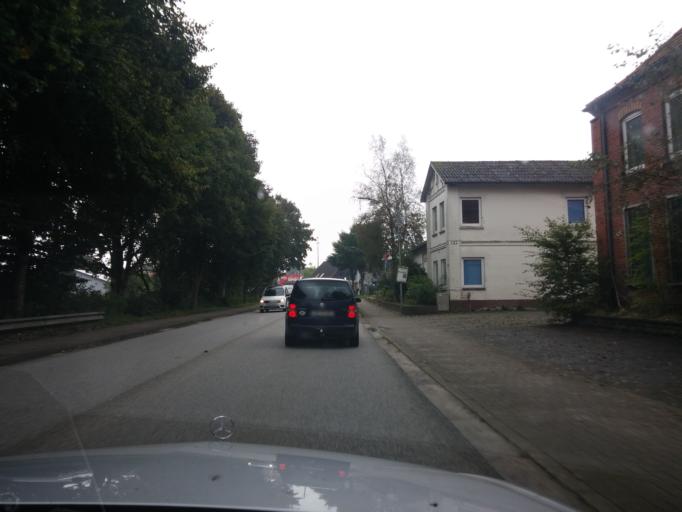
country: DE
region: Schleswig-Holstein
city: Treia
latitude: 54.5144
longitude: 9.3172
